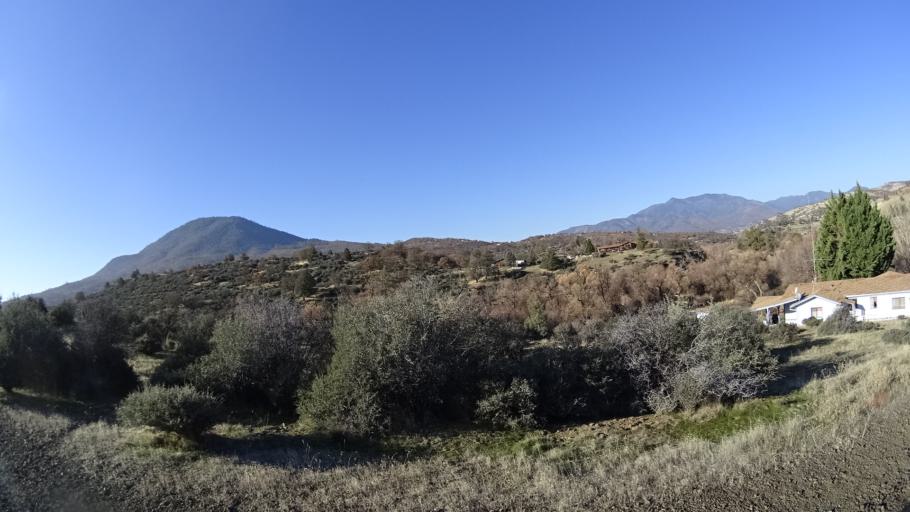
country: US
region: California
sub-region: Siskiyou County
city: Montague
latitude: 41.8978
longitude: -122.4901
